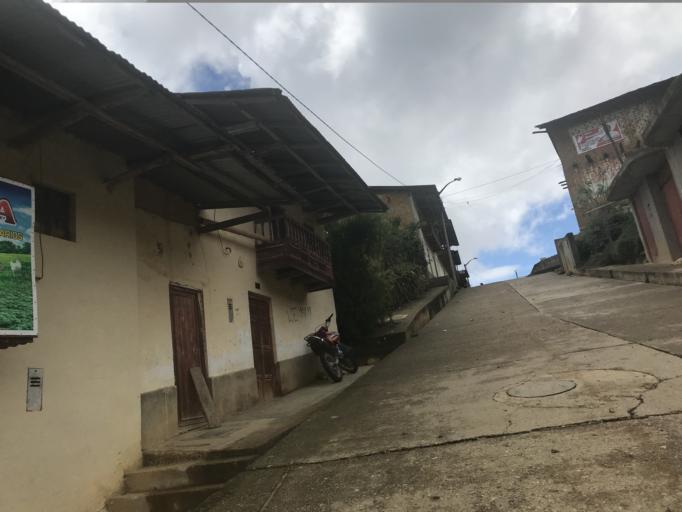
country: PE
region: Cajamarca
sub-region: Provincia de Chota
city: Querocoto
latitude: -6.3624
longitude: -79.0326
